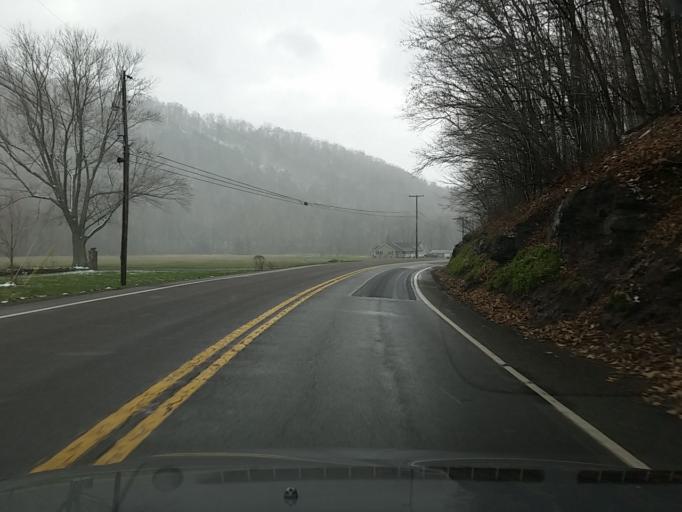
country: US
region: Pennsylvania
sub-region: Sullivan County
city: Laporte
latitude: 41.3448
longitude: -76.5578
